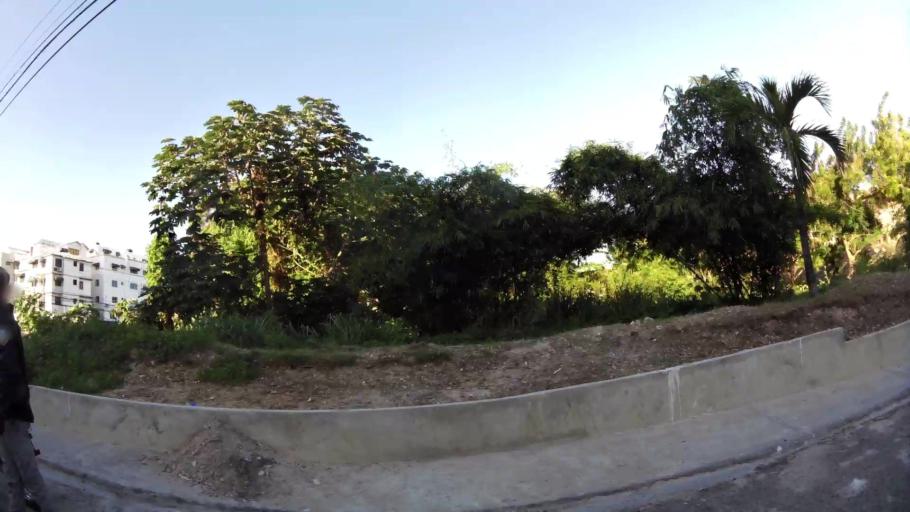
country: DO
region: Nacional
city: Santo Domingo
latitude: 18.4879
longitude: -69.9731
